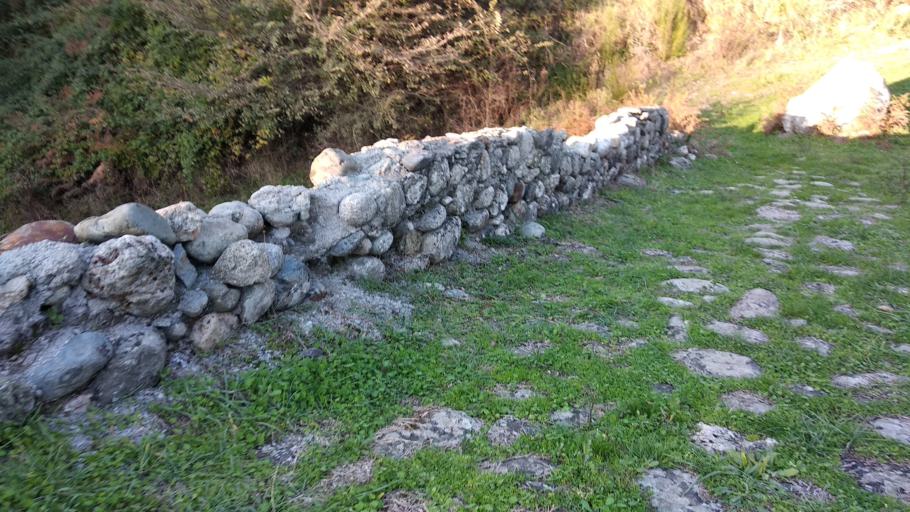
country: IT
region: Calabria
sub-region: Provincia di Cosenza
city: Altilia
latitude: 39.1330
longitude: 16.2746
